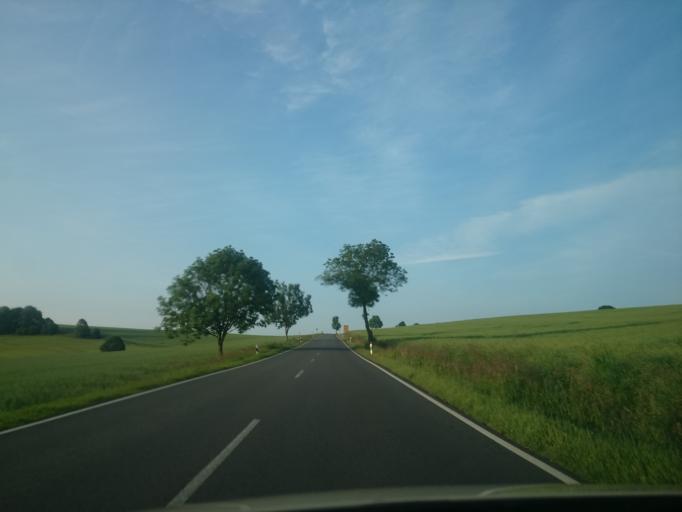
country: DE
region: Saxony
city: Grosshartmannsdorf
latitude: 50.7817
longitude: 13.3218
